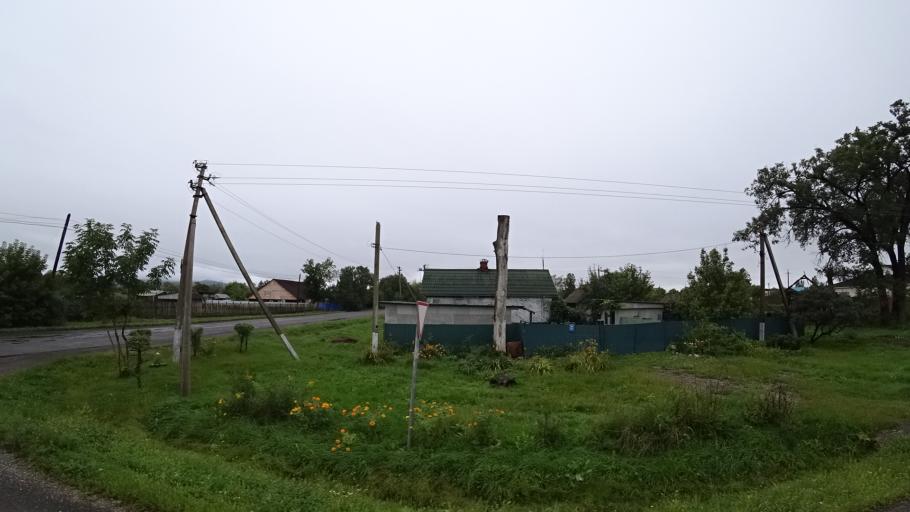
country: RU
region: Primorskiy
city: Monastyrishche
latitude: 44.2001
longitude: 132.4651
